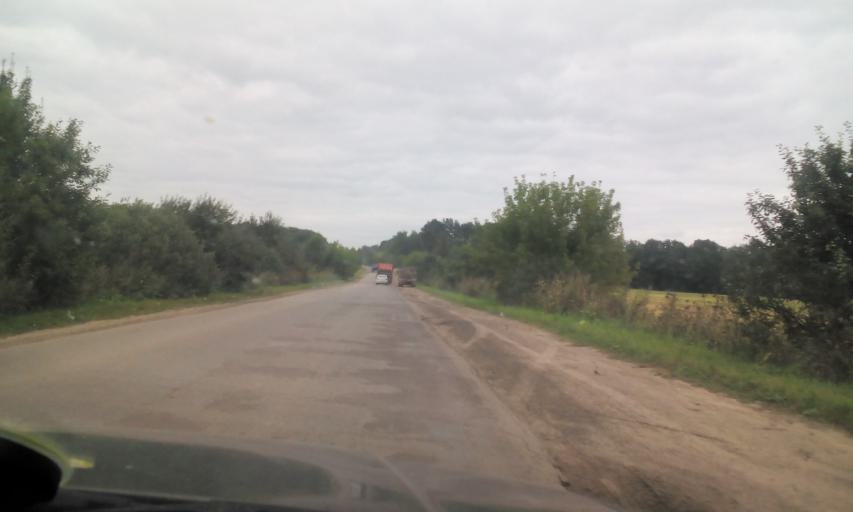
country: RU
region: Kaluga
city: Kaluga
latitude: 54.5207
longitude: 36.3761
